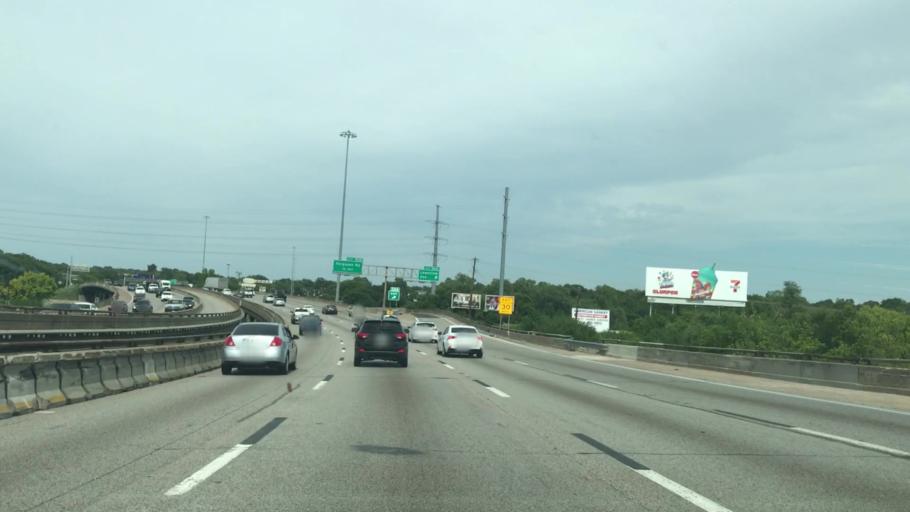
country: US
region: Texas
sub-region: Dallas County
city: Highland Park
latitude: 32.7914
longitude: -96.7298
